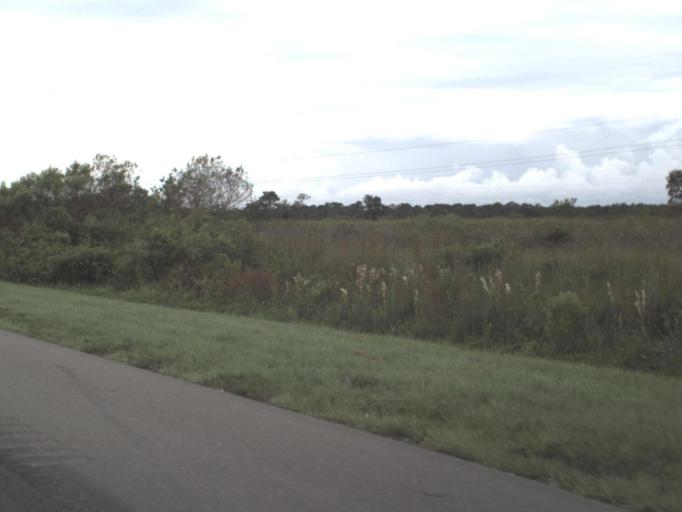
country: US
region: Florida
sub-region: Sarasota County
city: Laurel
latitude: 27.1767
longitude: -82.4356
